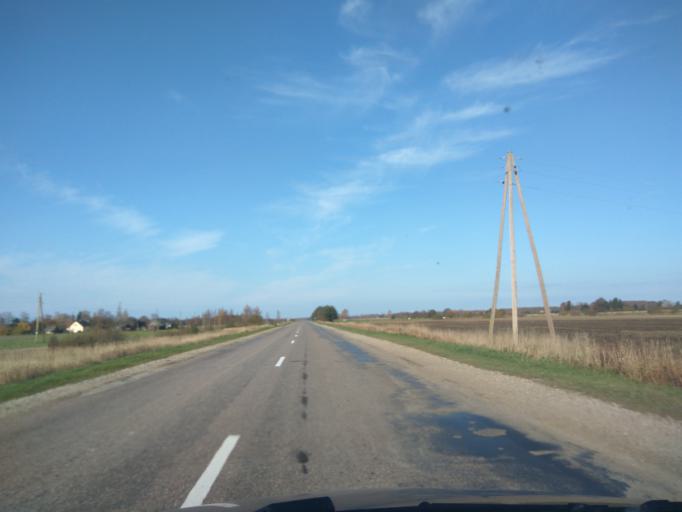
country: LV
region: Ventspils Rajons
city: Piltene
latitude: 57.2342
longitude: 21.5995
